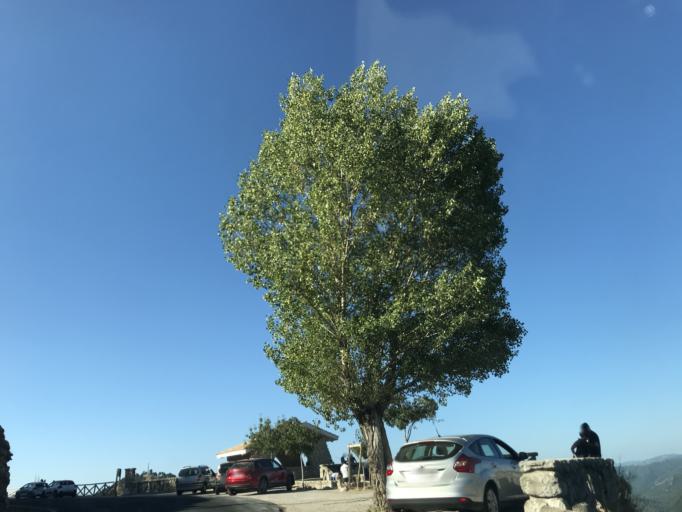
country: ES
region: Andalusia
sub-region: Provincia de Jaen
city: La Iruela
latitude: 37.9405
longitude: -2.9392
